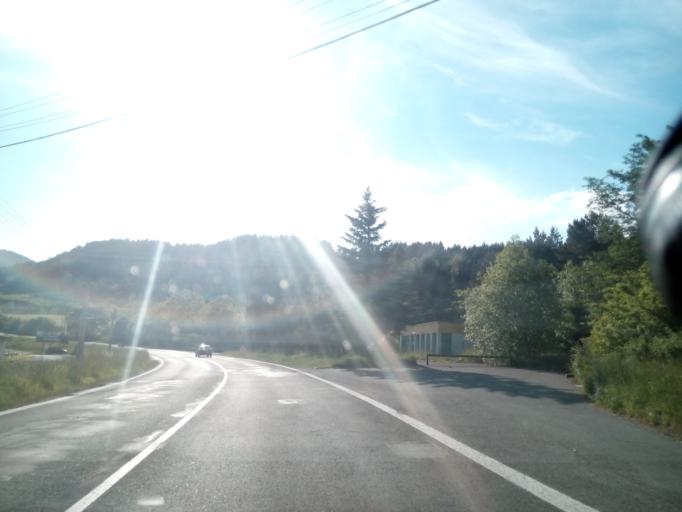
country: SK
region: Kosicky
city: Krompachy
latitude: 49.0139
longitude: 20.9501
